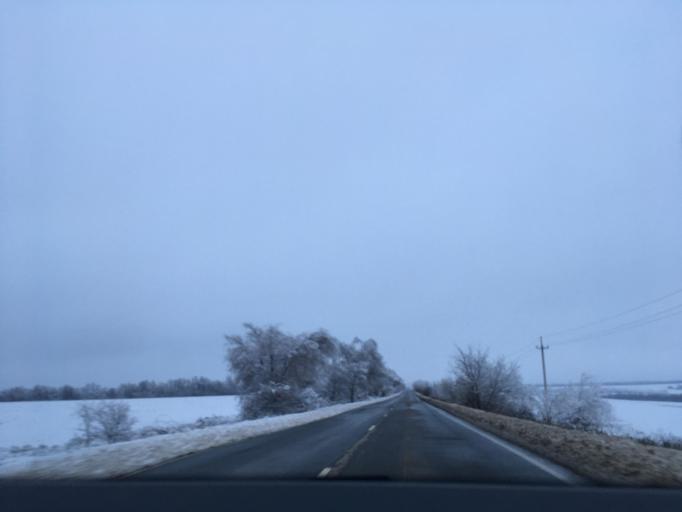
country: RU
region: Voronezj
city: Verkhniy Mamon
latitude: 50.0198
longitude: 40.1143
